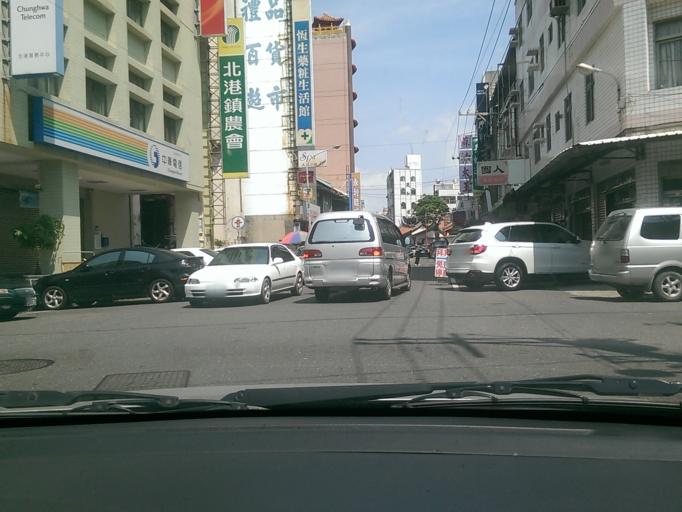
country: TW
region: Taiwan
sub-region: Chiayi
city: Taibao
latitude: 23.5688
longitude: 120.3038
